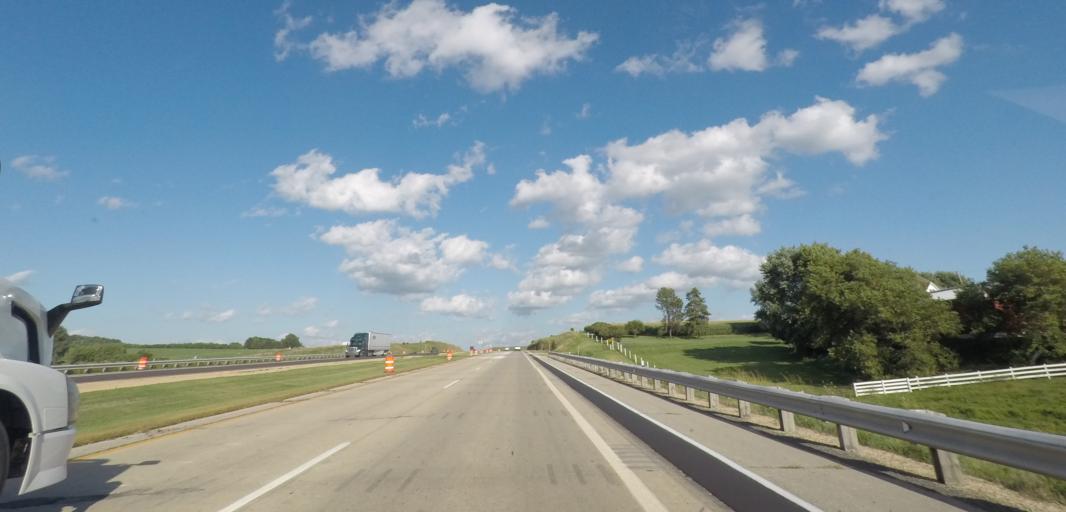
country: US
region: Wisconsin
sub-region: Iowa County
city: Barneveld
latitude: 43.0090
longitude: -89.8662
